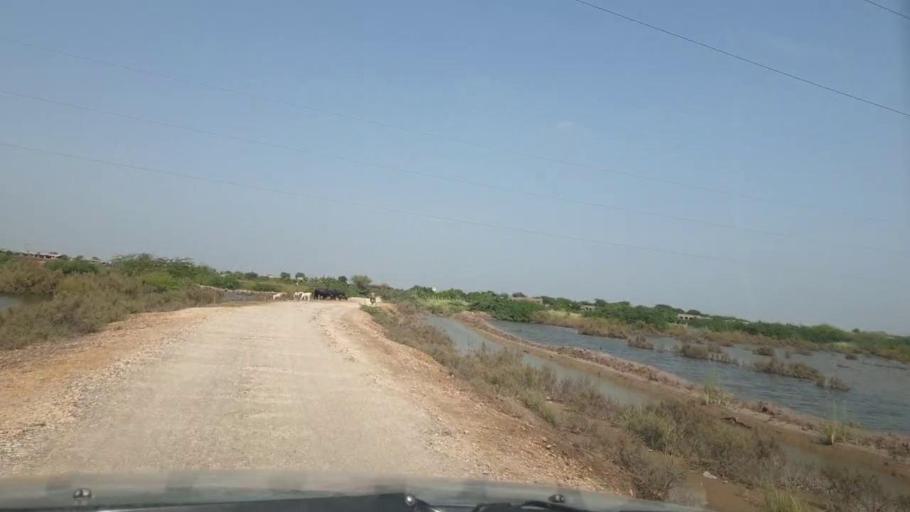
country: PK
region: Sindh
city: Tando Ghulam Ali
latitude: 25.0695
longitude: 68.8011
